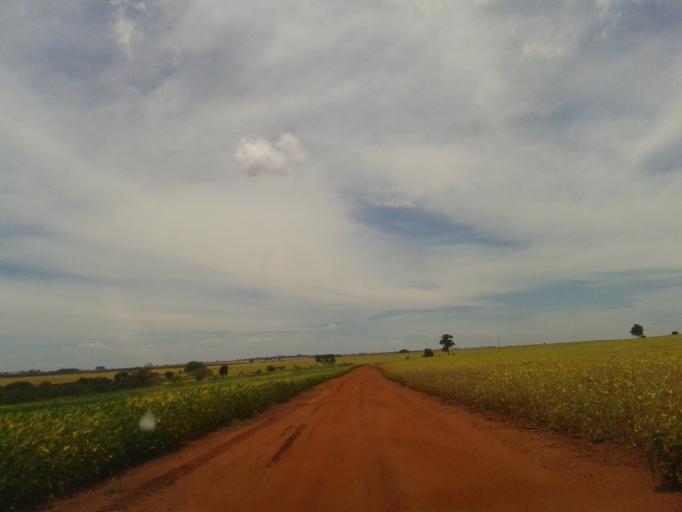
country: BR
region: Minas Gerais
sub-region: Capinopolis
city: Capinopolis
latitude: -18.6748
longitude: -49.7230
